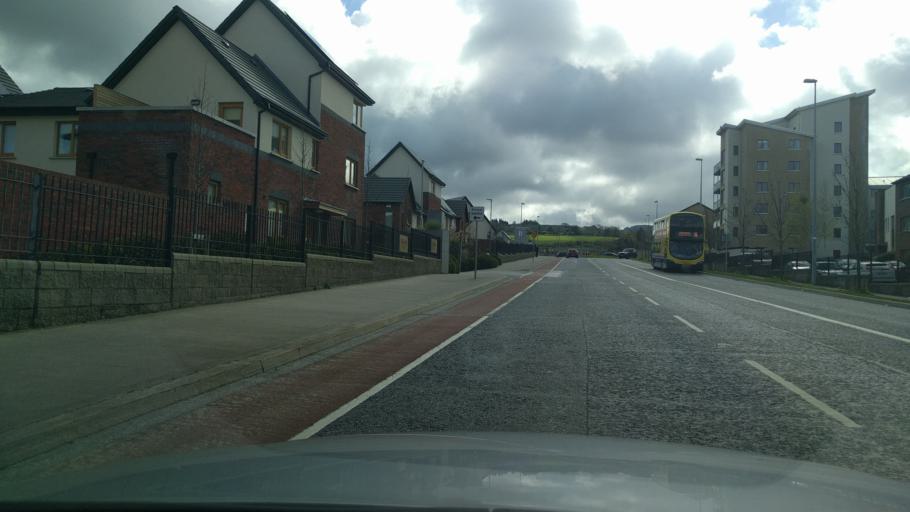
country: IE
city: Knocklyon
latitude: 53.2719
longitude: -6.3290
